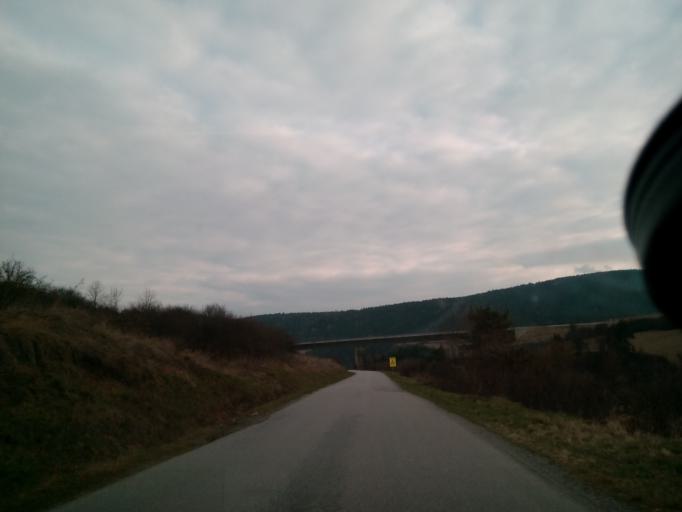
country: SK
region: Presovsky
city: Sabinov
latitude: 49.0311
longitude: 21.0190
